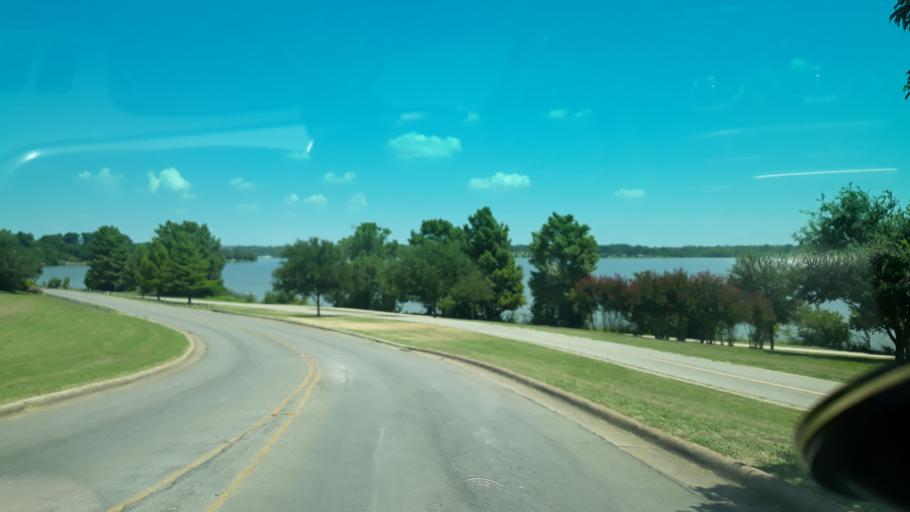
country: US
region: Texas
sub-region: Dallas County
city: Highland Park
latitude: 32.8272
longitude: -96.7298
